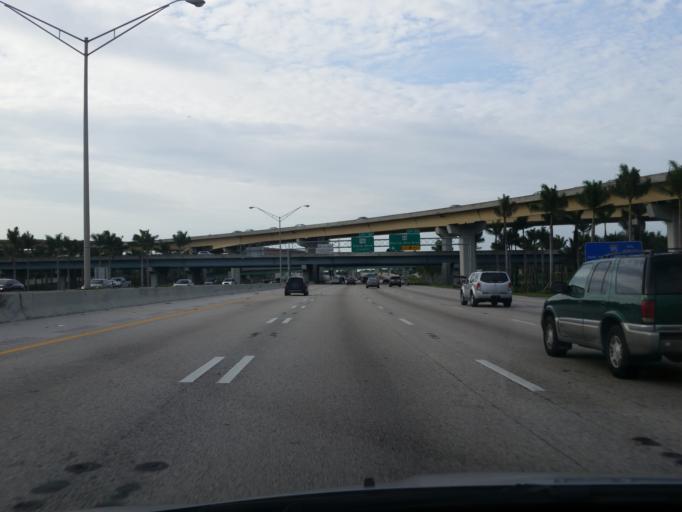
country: US
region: Florida
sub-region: Broward County
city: Dania Beach
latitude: 26.0802
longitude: -80.1687
